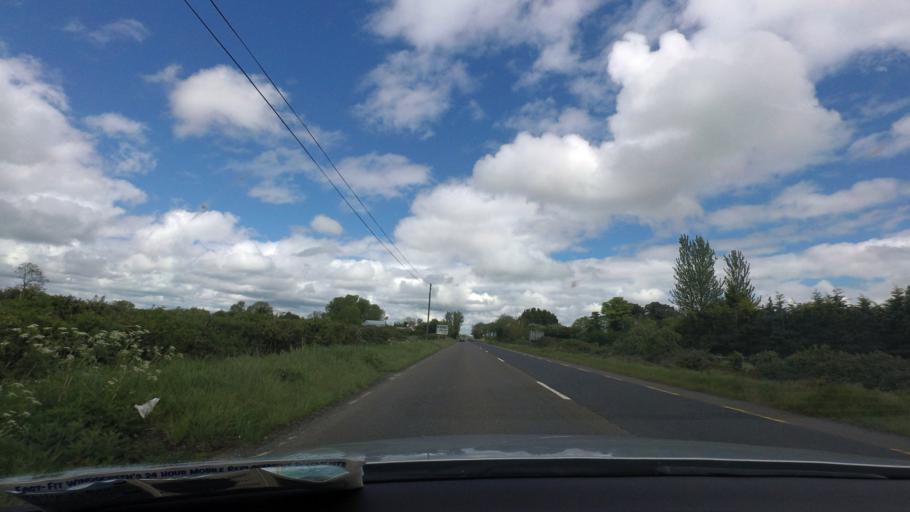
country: IE
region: Munster
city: Thurles
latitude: 52.5954
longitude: -7.8044
